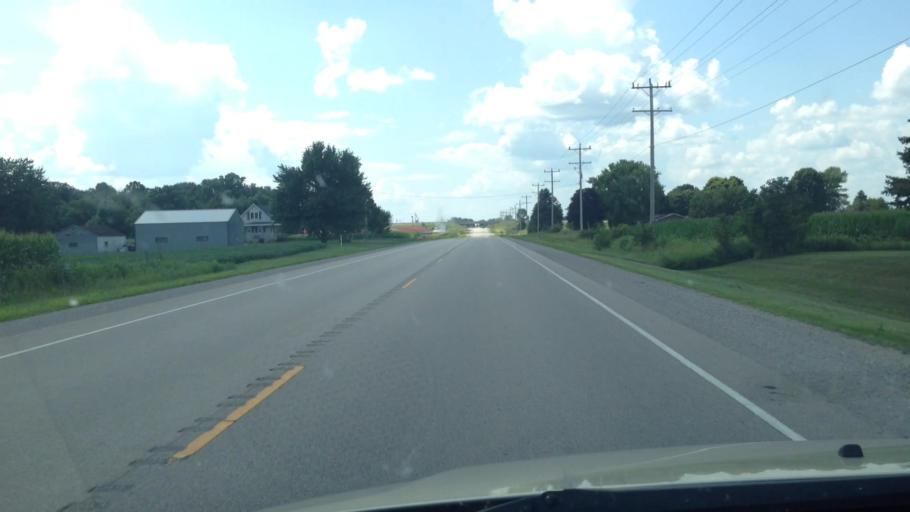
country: US
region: Wisconsin
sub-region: Brown County
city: Pulaski
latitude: 44.6735
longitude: -88.2959
